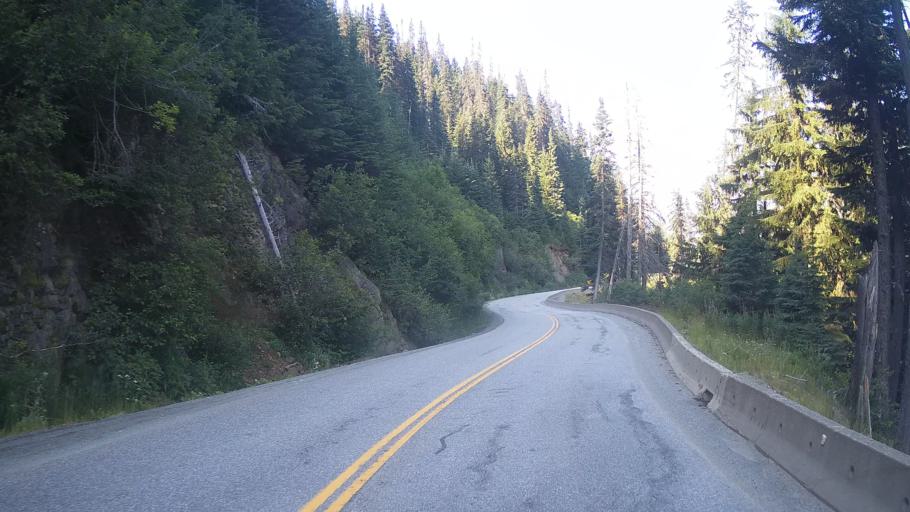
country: CA
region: British Columbia
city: Lillooet
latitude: 50.4146
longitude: -122.2822
